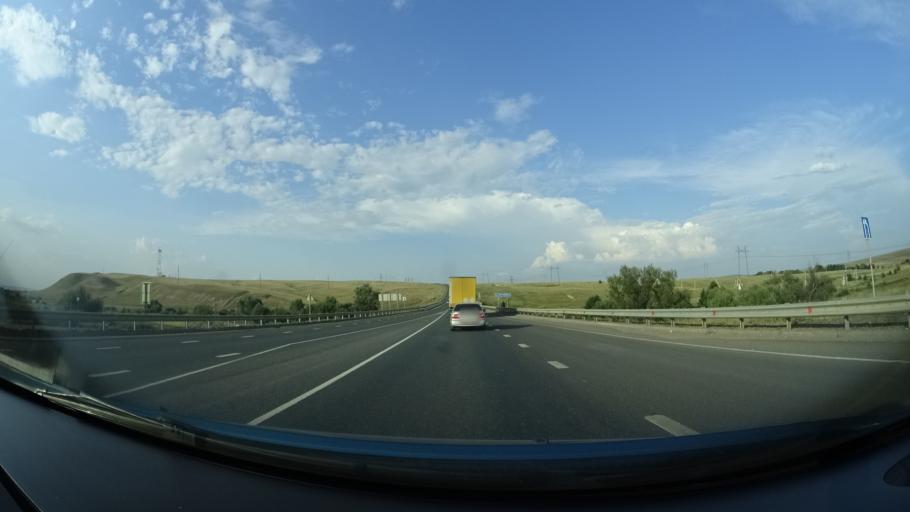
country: RU
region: Samara
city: Krasnyy Yar
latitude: 53.6900
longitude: 50.7922
